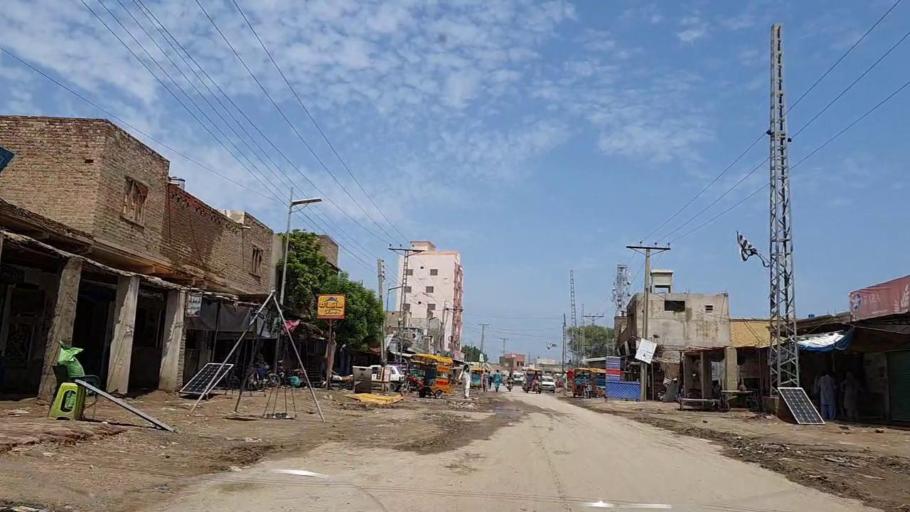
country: PK
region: Sindh
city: Naushahro Firoz
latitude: 26.8424
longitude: 68.1170
